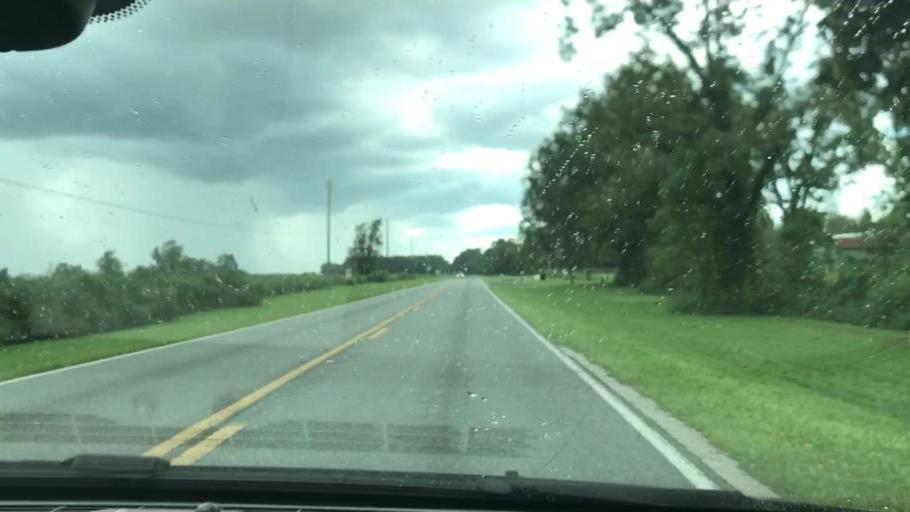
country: US
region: Florida
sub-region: Madison County
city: Madison
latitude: 30.4122
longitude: -83.3002
